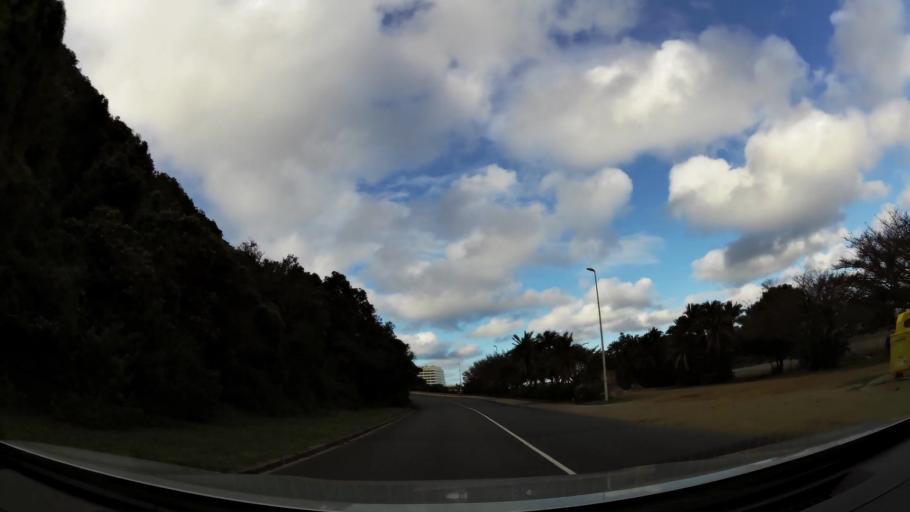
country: ZA
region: Western Cape
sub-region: Eden District Municipality
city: Plettenberg Bay
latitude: -34.0606
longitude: 23.3741
